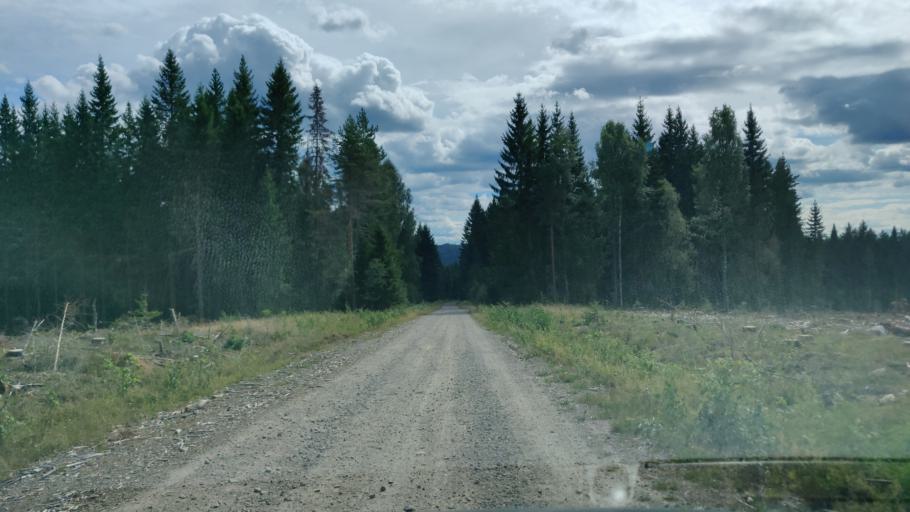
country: SE
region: Vaermland
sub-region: Hagfors Kommun
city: Hagfors
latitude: 60.0072
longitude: 13.7272
